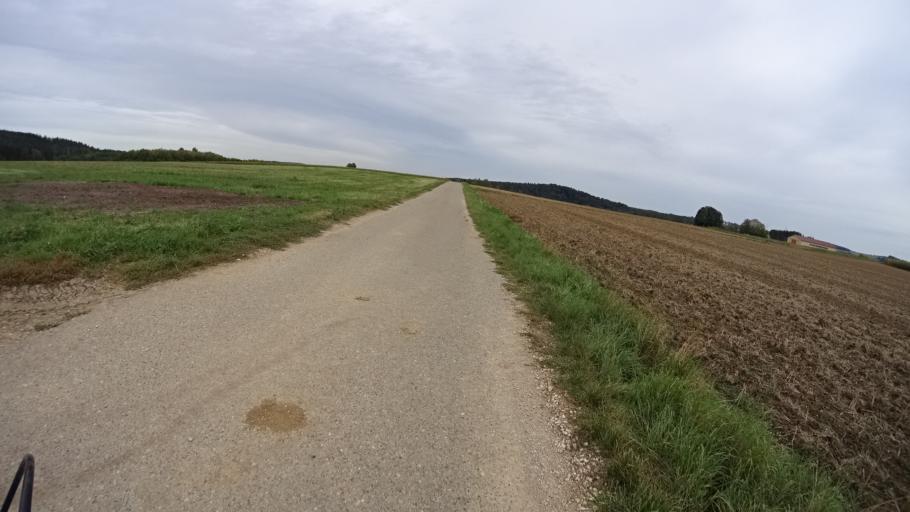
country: DE
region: Bavaria
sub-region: Upper Bavaria
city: Hitzhofen
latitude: 48.8762
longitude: 11.3353
